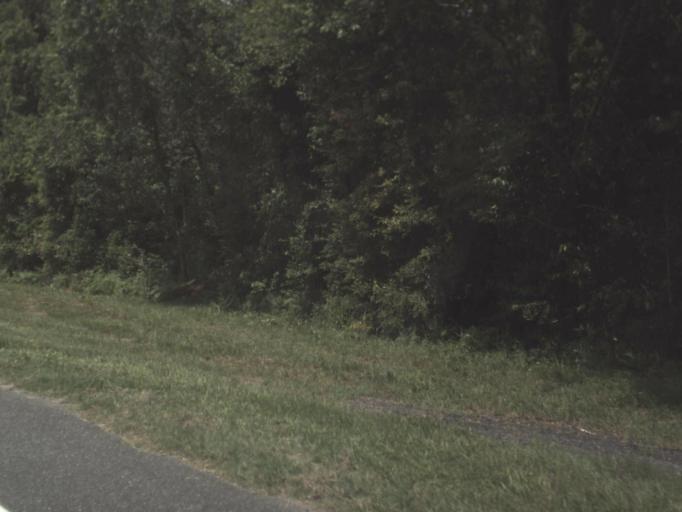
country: US
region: Florida
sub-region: Suwannee County
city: Wellborn
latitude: 30.0723
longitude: -82.9442
